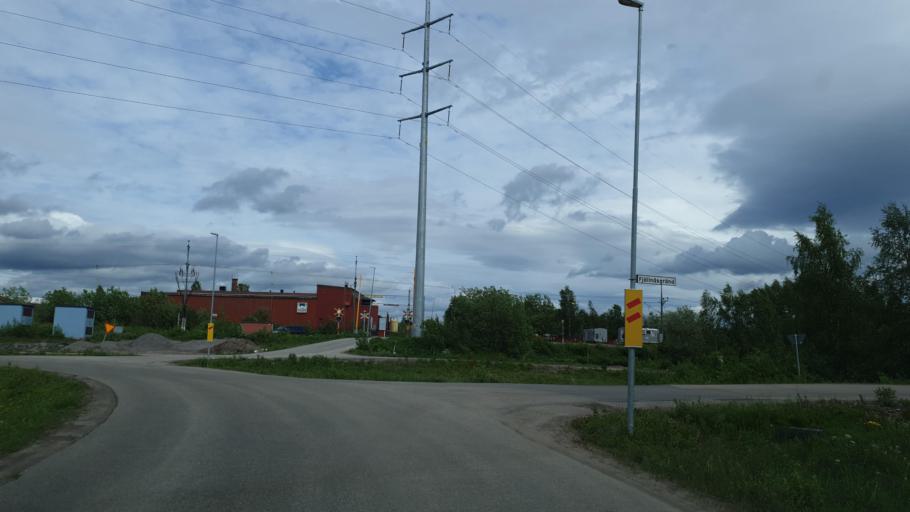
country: SE
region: Norrbotten
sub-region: Gallivare Kommun
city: Gaellivare
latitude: 67.1273
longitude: 20.6575
